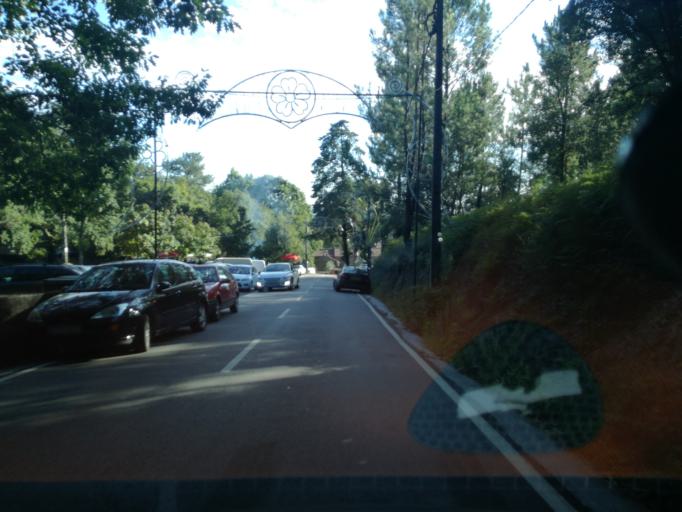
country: PT
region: Porto
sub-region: Santo Tirso
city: Sao Miguel do Couto
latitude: 41.3055
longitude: -8.4499
